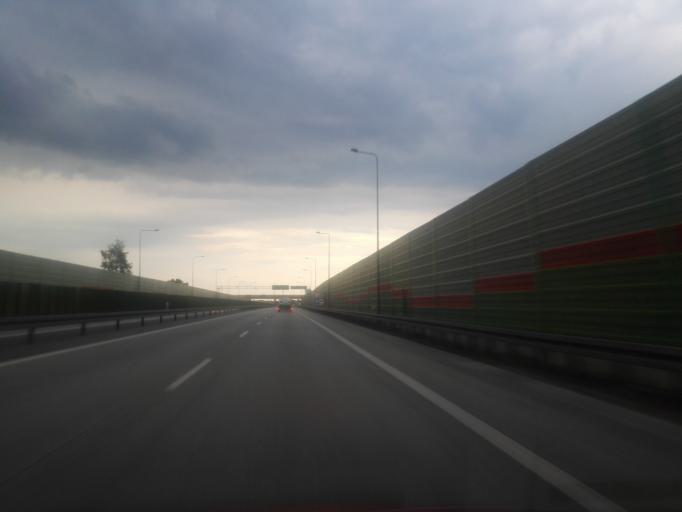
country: PL
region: Lodz Voivodeship
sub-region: Piotrkow Trybunalski
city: Piotrkow Trybunalski
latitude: 51.4422
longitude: 19.6634
